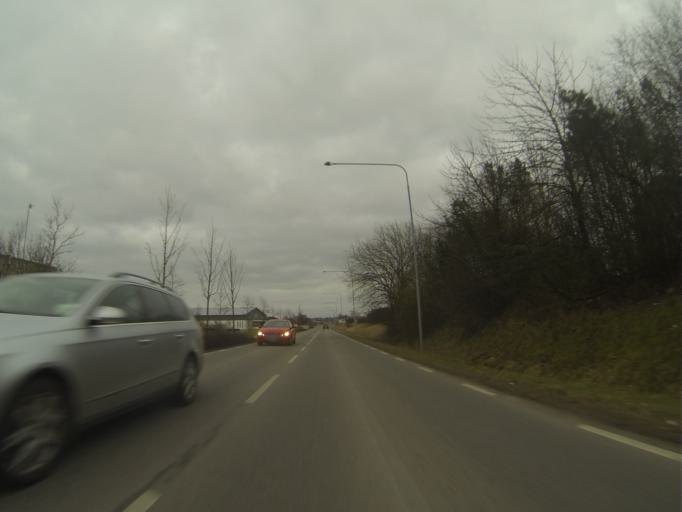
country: SE
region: Skane
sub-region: Svedala Kommun
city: Svedala
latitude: 55.5154
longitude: 13.2402
